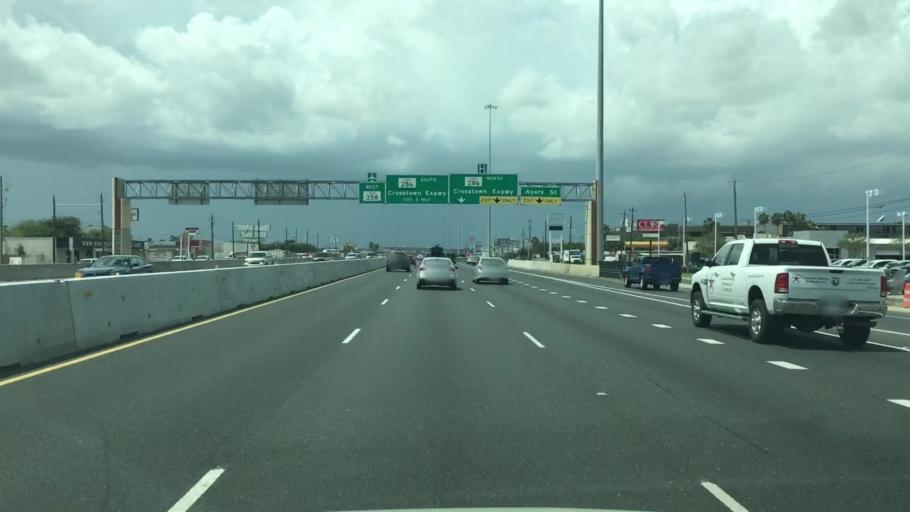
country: US
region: Texas
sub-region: Nueces County
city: Corpus Christi
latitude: 27.7302
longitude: -97.4162
